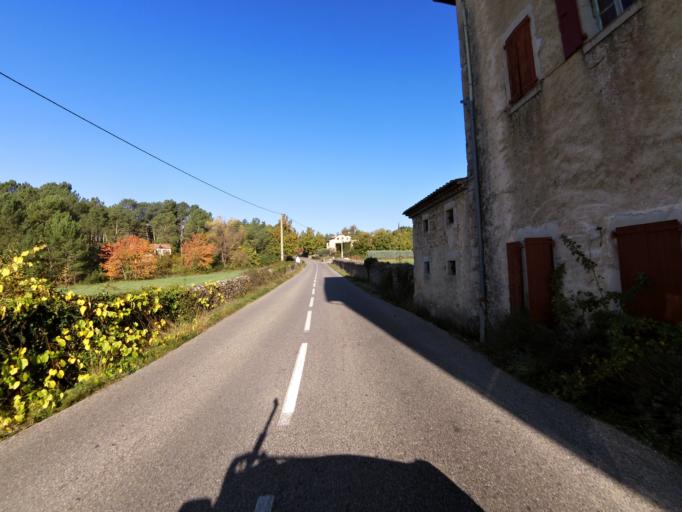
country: FR
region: Rhone-Alpes
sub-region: Departement de l'Ardeche
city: Lablachere
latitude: 44.4697
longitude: 4.2034
